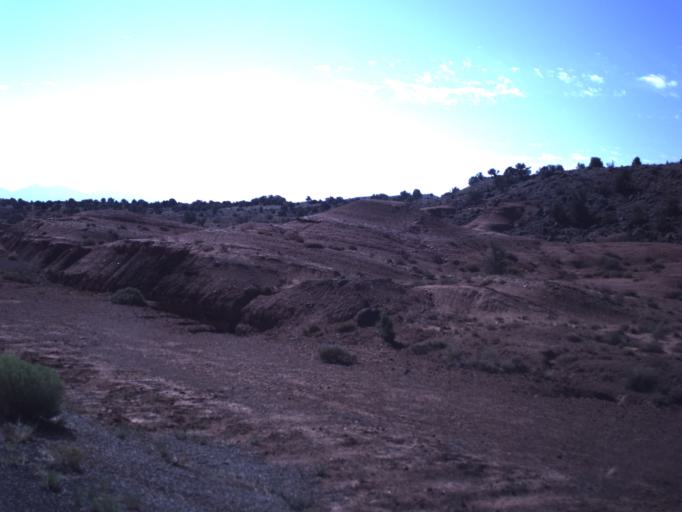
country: US
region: Utah
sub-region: Wayne County
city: Loa
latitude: 38.3229
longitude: -111.3435
